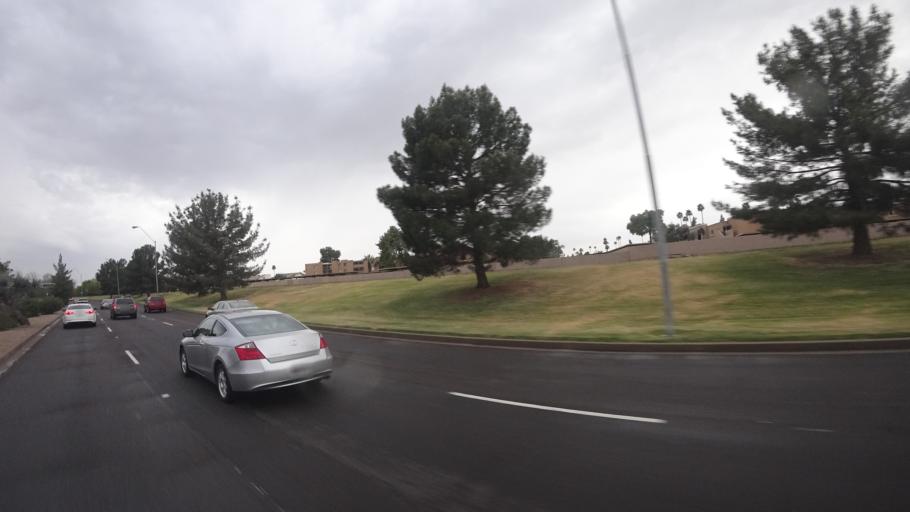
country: US
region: Arizona
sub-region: Maricopa County
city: Scottsdale
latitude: 33.5004
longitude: -111.9092
